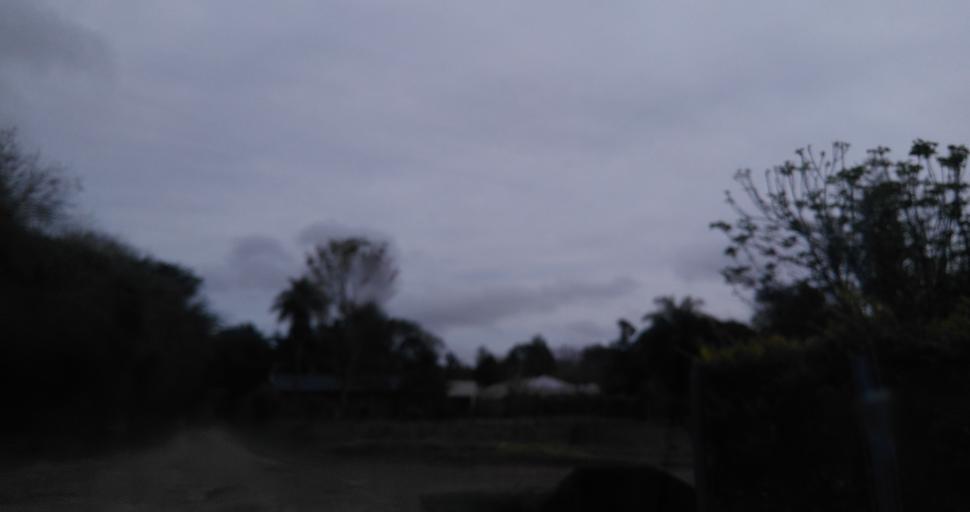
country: AR
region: Chaco
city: Colonia Benitez
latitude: -27.3261
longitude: -58.9557
